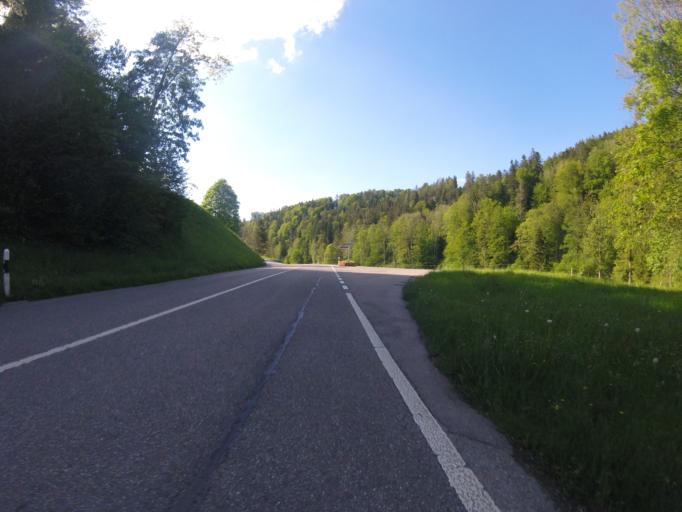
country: CH
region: Saint Gallen
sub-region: Wahlkreis Toggenburg
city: Mogelsberg
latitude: 47.3627
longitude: 9.1505
